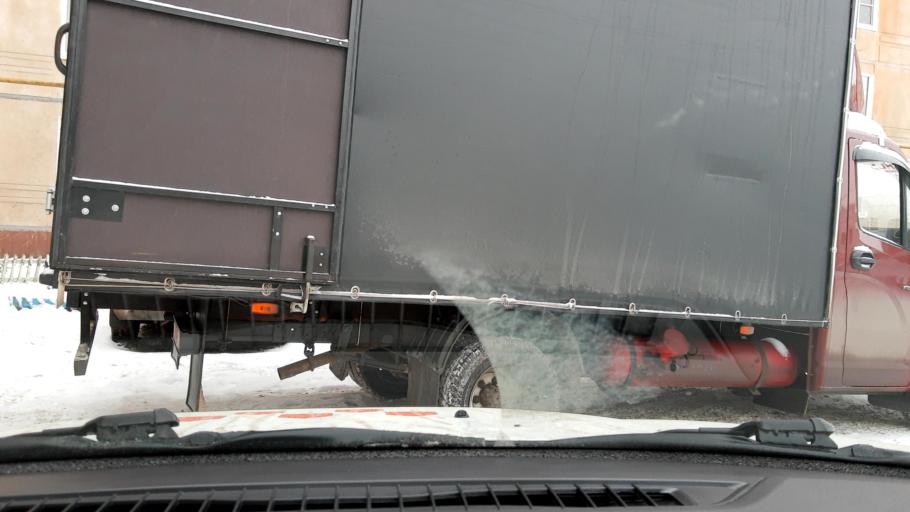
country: RU
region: Nizjnij Novgorod
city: Pyra
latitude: 56.2275
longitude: 43.3755
